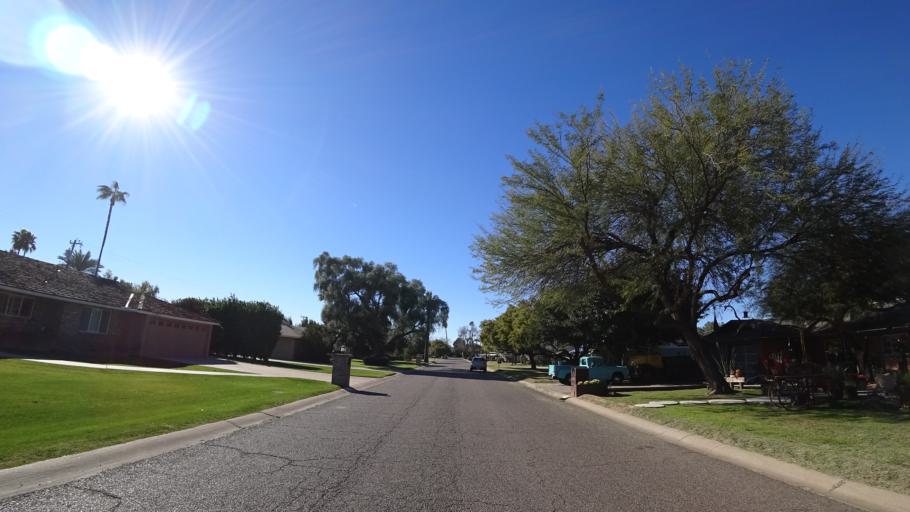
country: US
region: Arizona
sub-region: Maricopa County
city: Phoenix
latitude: 33.5496
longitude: -112.0705
